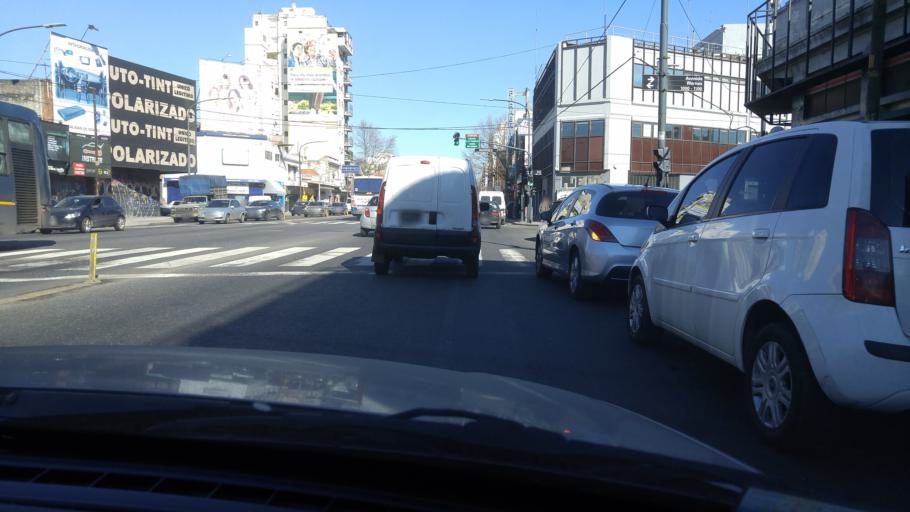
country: AR
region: Buenos Aires F.D.
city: Colegiales
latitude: -34.5992
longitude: -58.4507
